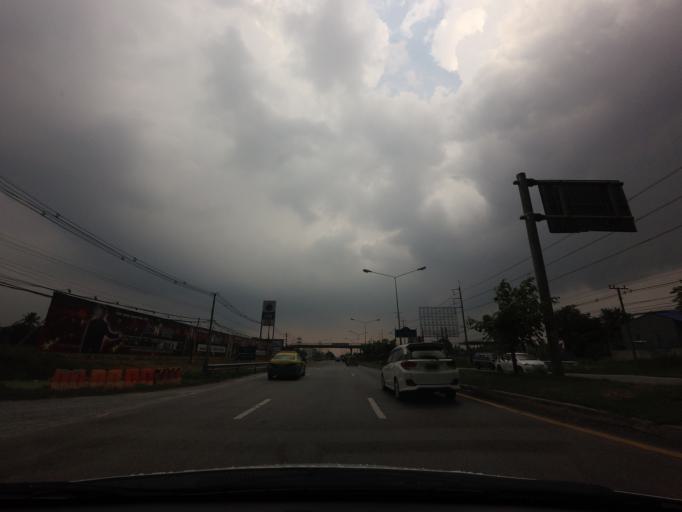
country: TH
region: Nakhon Pathom
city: Salaya
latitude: 13.7855
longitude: 100.2710
